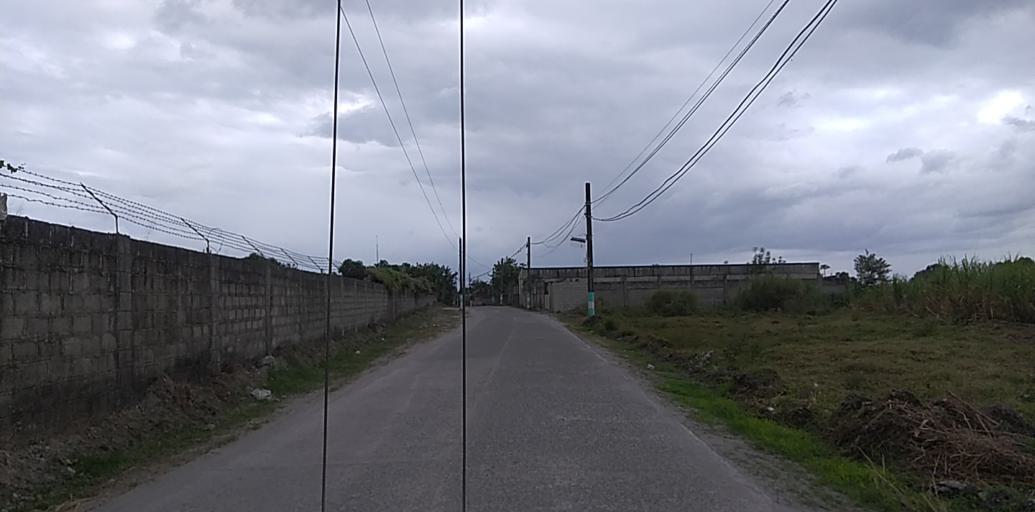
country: PH
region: Central Luzon
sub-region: Province of Pampanga
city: Pio
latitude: 15.0454
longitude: 120.5344
